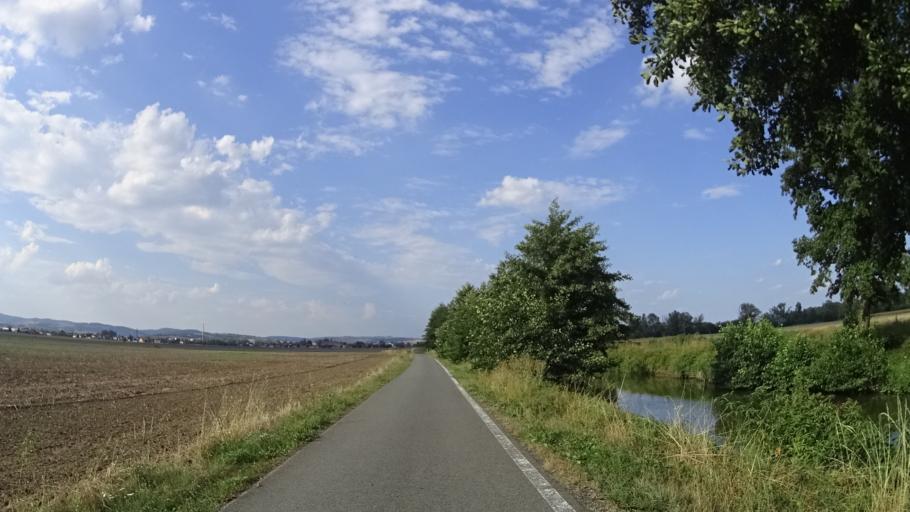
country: CZ
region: Zlin
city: Babice
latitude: 49.1062
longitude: 17.4780
